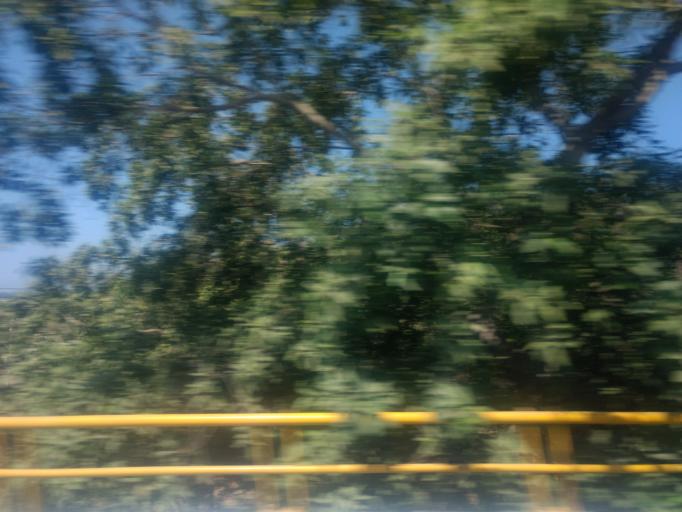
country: MX
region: Colima
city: El Colomo
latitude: 19.0511
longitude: -104.2684
